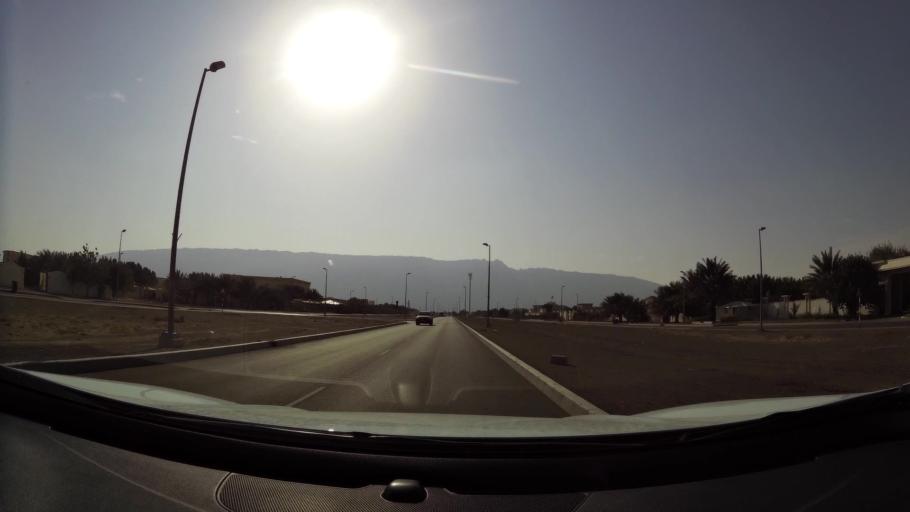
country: AE
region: Abu Dhabi
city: Al Ain
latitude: 24.0662
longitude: 55.8468
